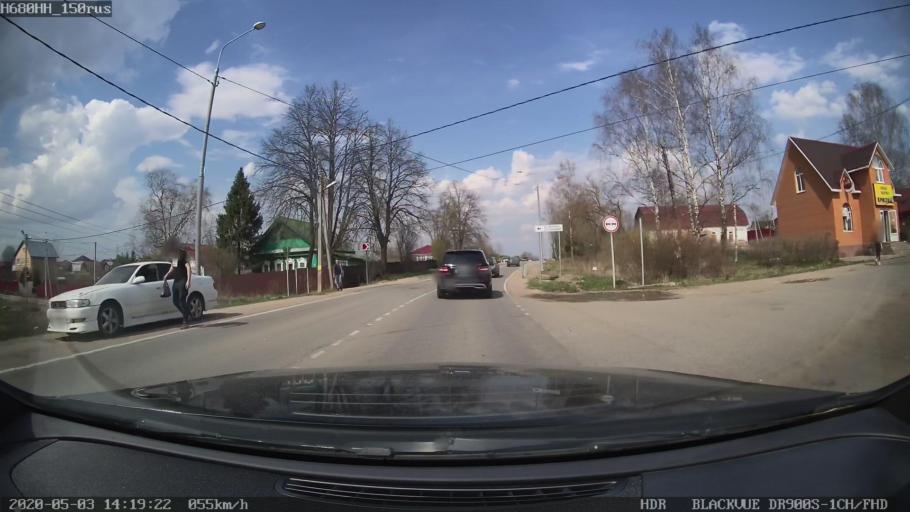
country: RU
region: Moskovskaya
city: Solnechnogorsk
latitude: 56.2309
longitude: 36.9677
